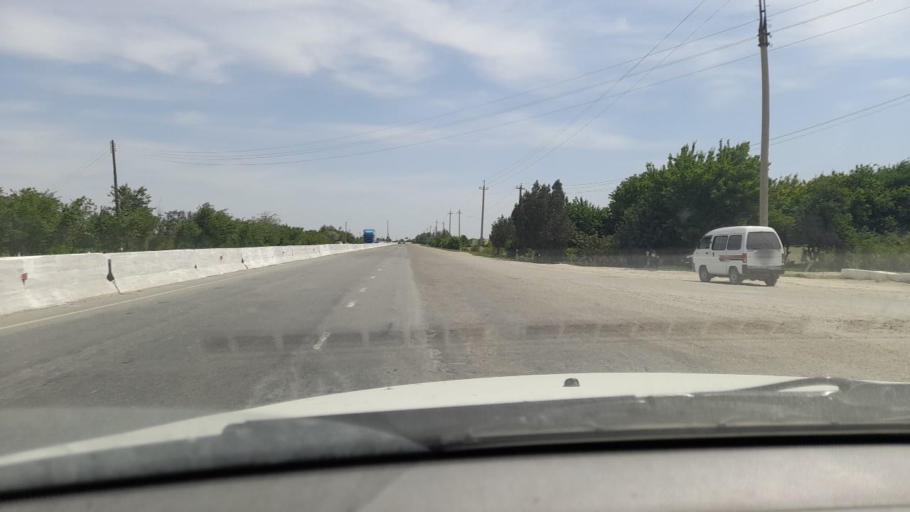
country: UZ
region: Bukhara
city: Ghijduwon
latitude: 40.0904
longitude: 64.6237
